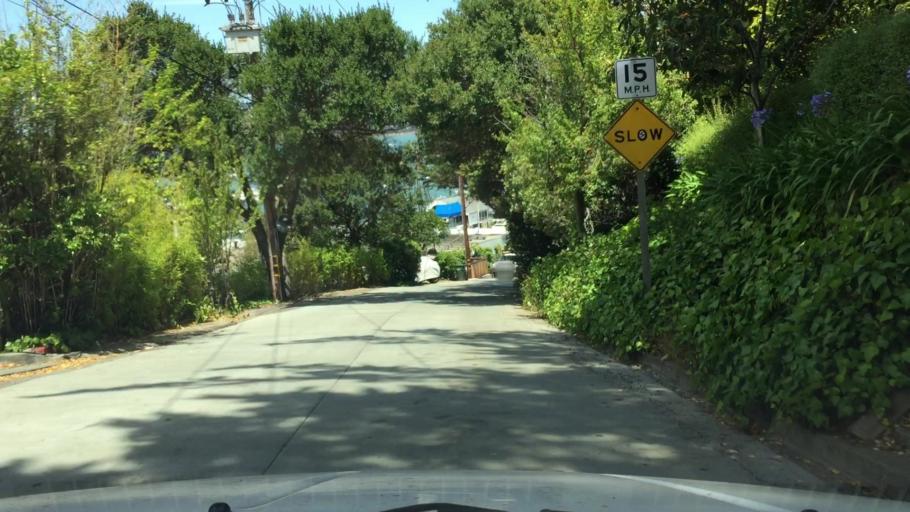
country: US
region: California
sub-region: Marin County
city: Sausalito
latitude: 37.8572
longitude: -122.4842
